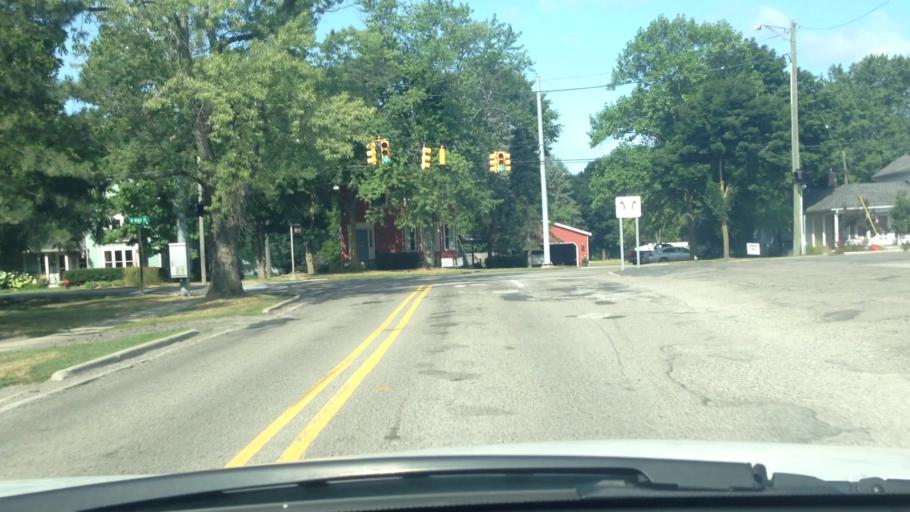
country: US
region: Michigan
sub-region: Oakland County
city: Clarkston
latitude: 42.7399
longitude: -83.4187
